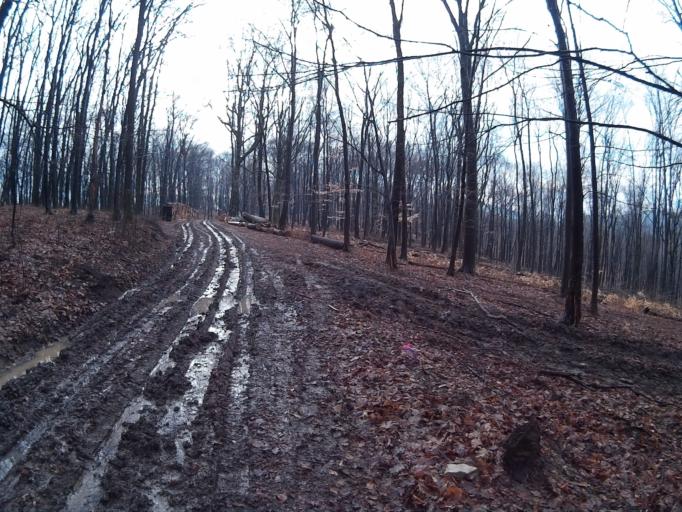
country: HU
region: Borsod-Abauj-Zemplen
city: Satoraljaujhely
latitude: 48.4226
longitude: 21.5770
